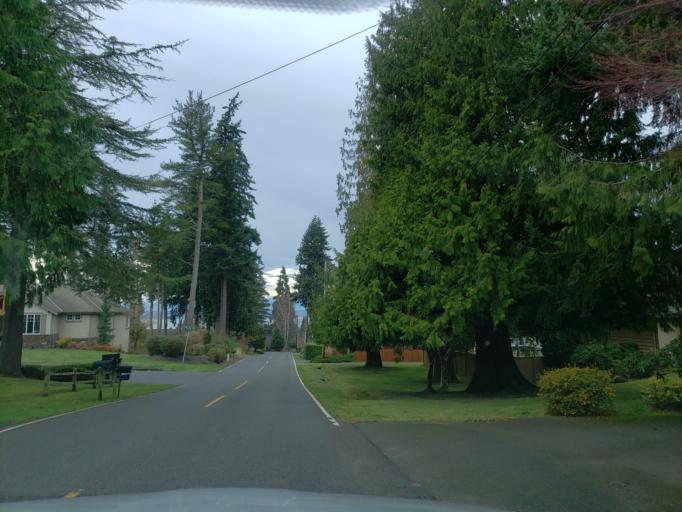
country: US
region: Washington
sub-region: Snohomish County
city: Edmonds
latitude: 47.8287
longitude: -122.3543
